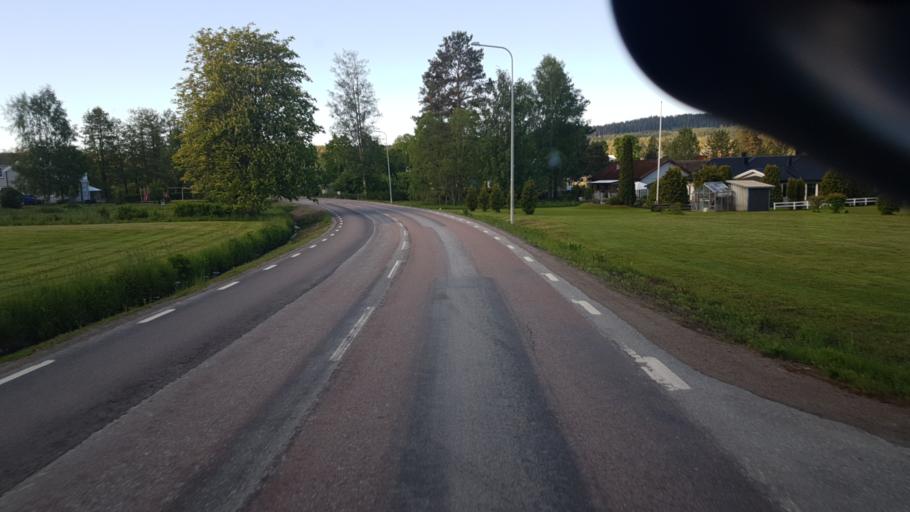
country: SE
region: Vaermland
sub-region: Arvika Kommun
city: Arvika
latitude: 59.5536
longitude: 12.5619
